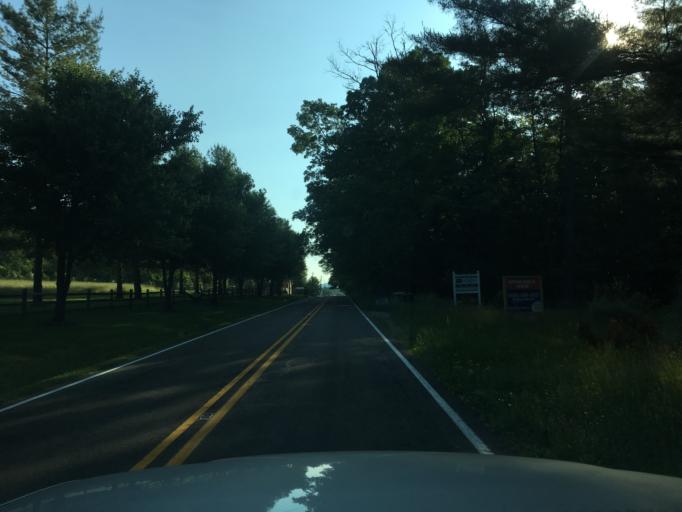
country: US
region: North Carolina
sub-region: Henderson County
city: Hoopers Creek
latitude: 35.4766
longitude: -82.4495
